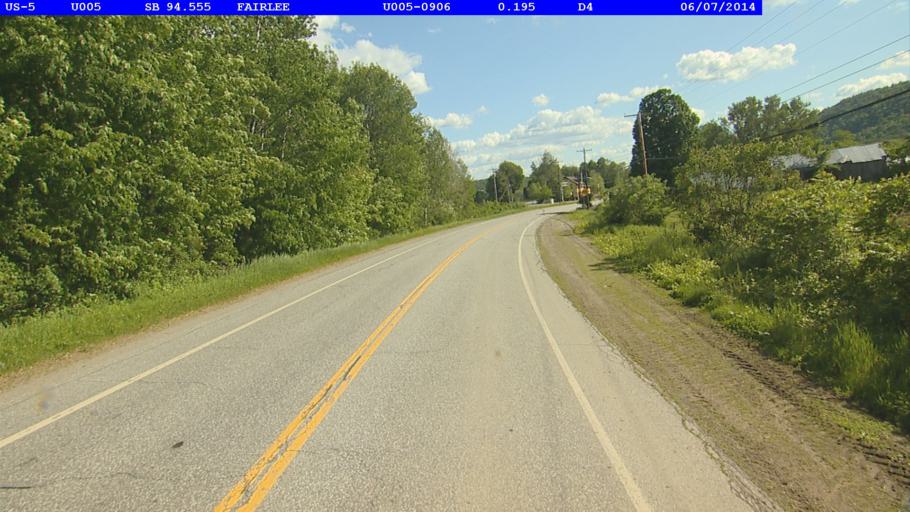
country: US
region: New Hampshire
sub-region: Grafton County
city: Orford
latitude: 43.8769
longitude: -72.1762
